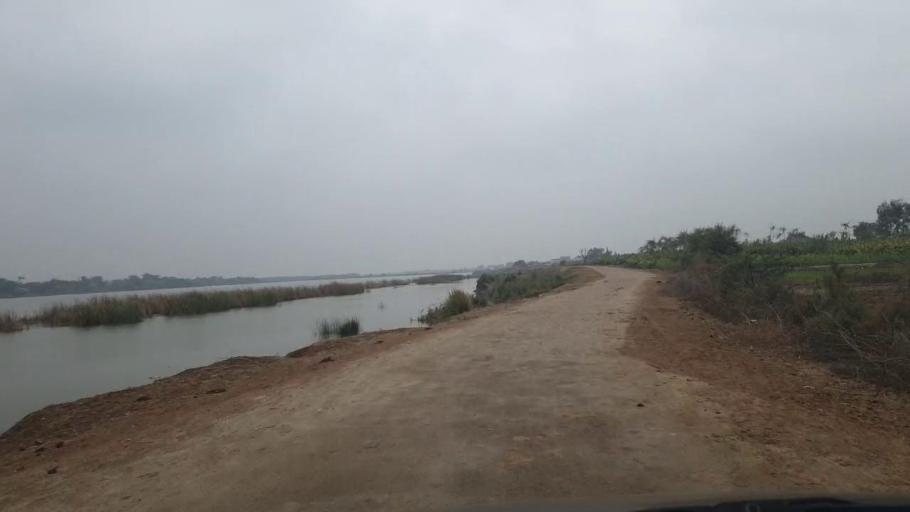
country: PK
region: Sindh
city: Tando Adam
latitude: 25.8309
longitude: 68.7186
